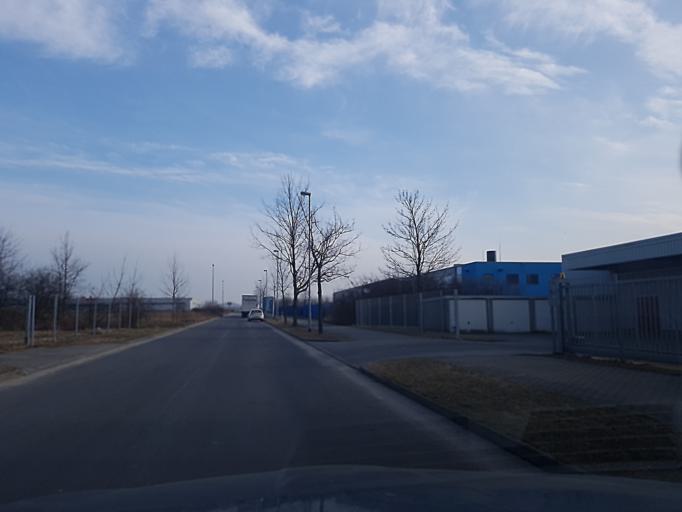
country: DE
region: Brandenburg
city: Finsterwalde
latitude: 51.6341
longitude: 13.7424
